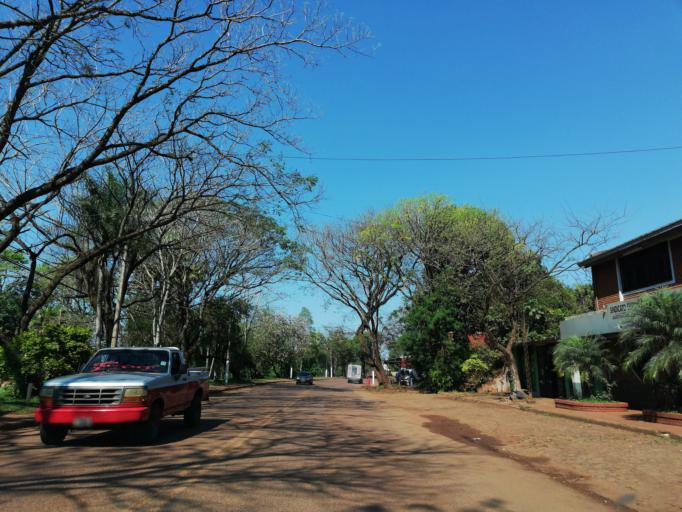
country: AR
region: Misiones
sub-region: Departamento de Eldorado
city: Eldorado
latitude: -26.4074
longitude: -54.6412
